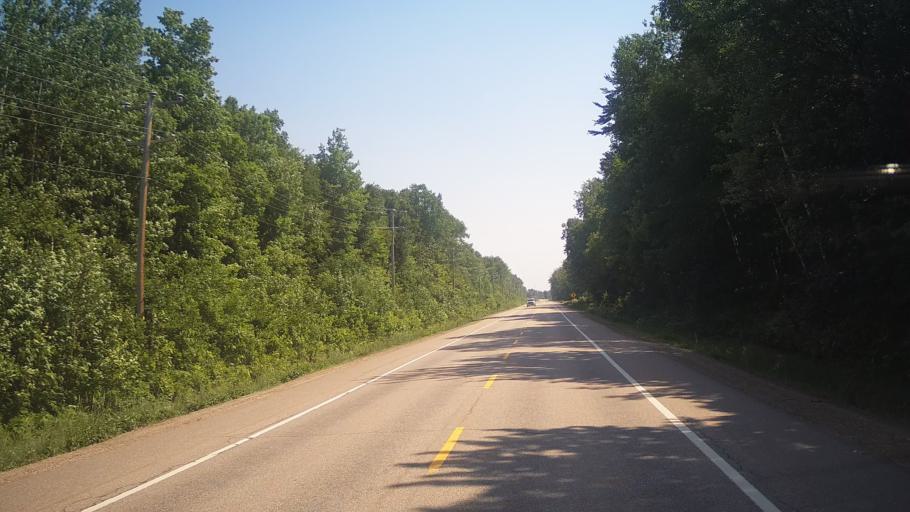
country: CA
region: Ontario
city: Pembroke
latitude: 45.8404
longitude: -77.0134
